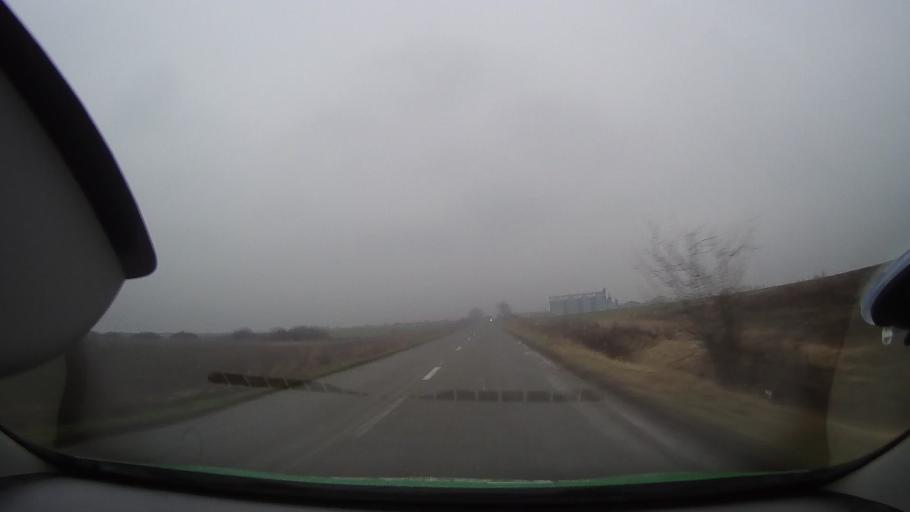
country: RO
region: Bihor
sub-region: Comuna Tulca
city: Tulca
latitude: 46.7953
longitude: 21.7328
